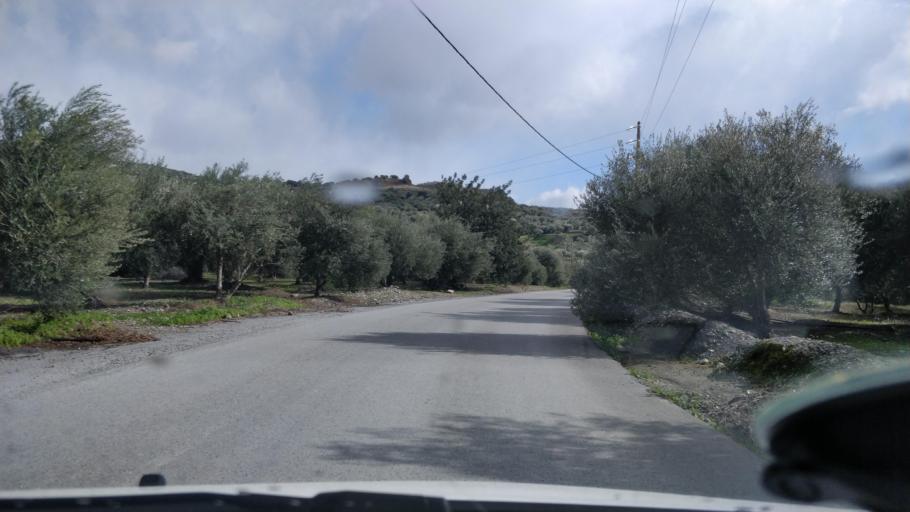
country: GR
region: Crete
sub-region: Nomos Lasithiou
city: Gra Liyia
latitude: 34.9957
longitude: 25.5043
